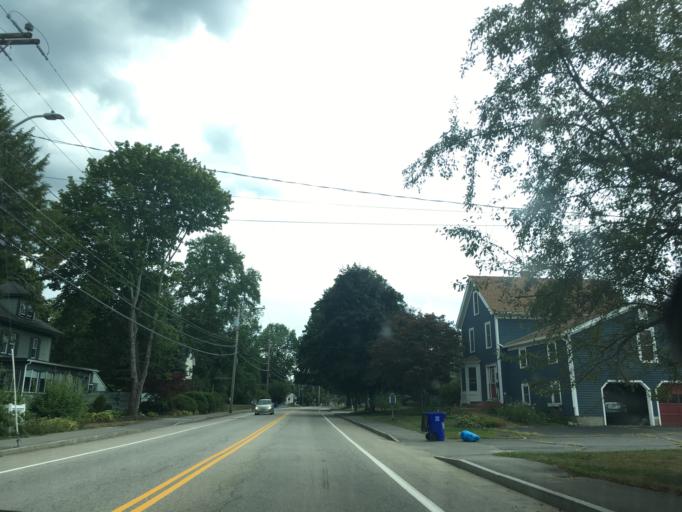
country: US
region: New Hampshire
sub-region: Rockingham County
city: Exeter
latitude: 42.9851
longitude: -70.9628
